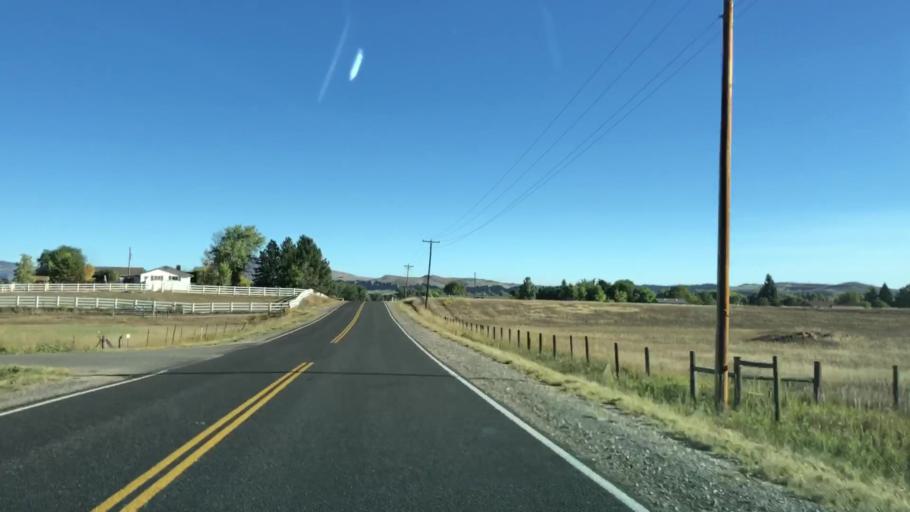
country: US
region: Colorado
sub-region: Larimer County
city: Loveland
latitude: 40.3876
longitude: -105.1633
